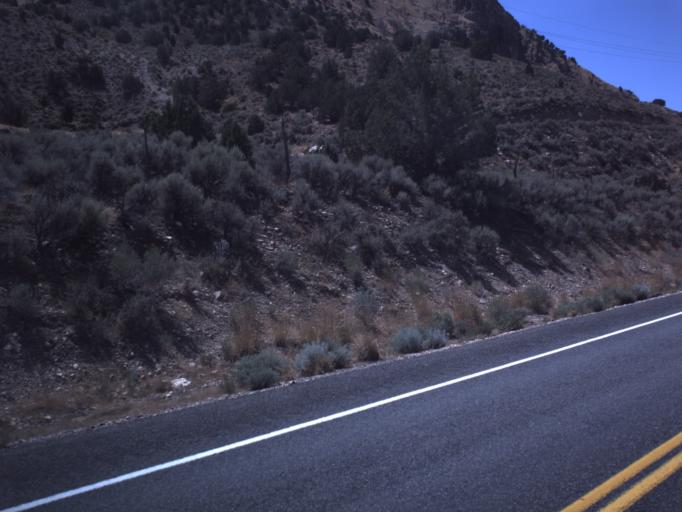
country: US
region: Utah
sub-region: Juab County
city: Nephi
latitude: 39.5579
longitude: -112.2082
